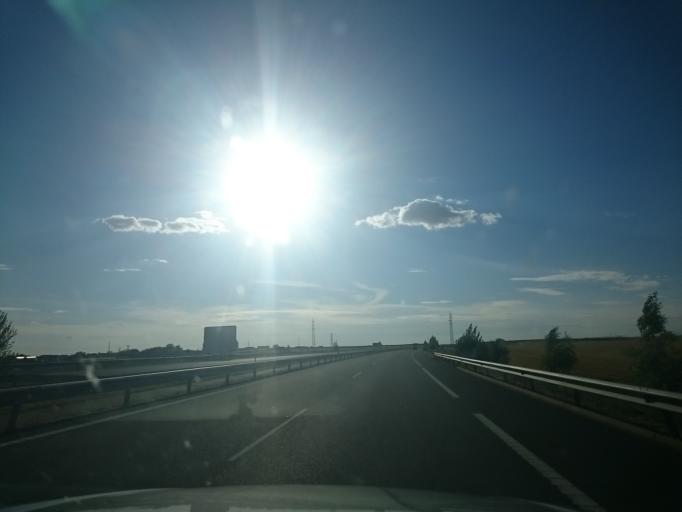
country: ES
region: Castille and Leon
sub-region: Provincia de Burgos
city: Melgar de Fernamental
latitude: 42.4043
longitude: -4.2256
